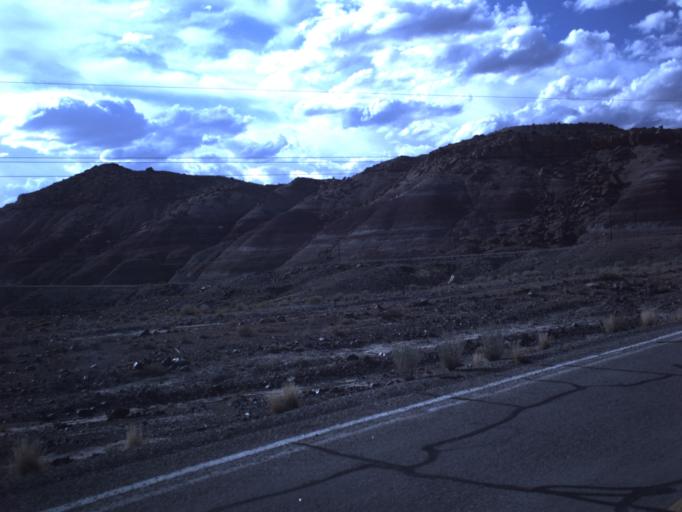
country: US
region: Utah
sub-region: San Juan County
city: Blanding
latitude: 37.3229
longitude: -109.3202
